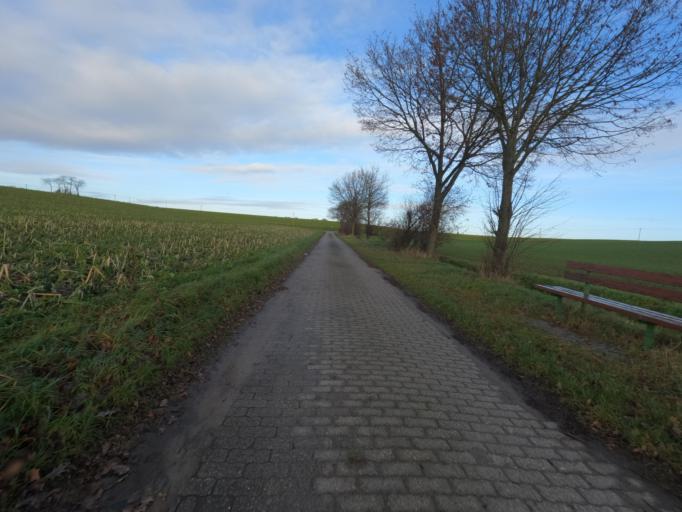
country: DE
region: North Rhine-Westphalia
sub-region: Regierungsbezirk Koln
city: Titz
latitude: 51.0162
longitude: 6.3747
